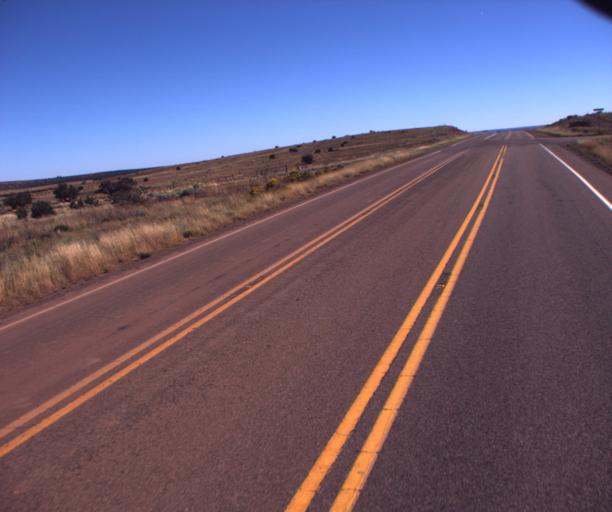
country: US
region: Arizona
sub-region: Navajo County
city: Snowflake
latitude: 34.5127
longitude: -110.1503
